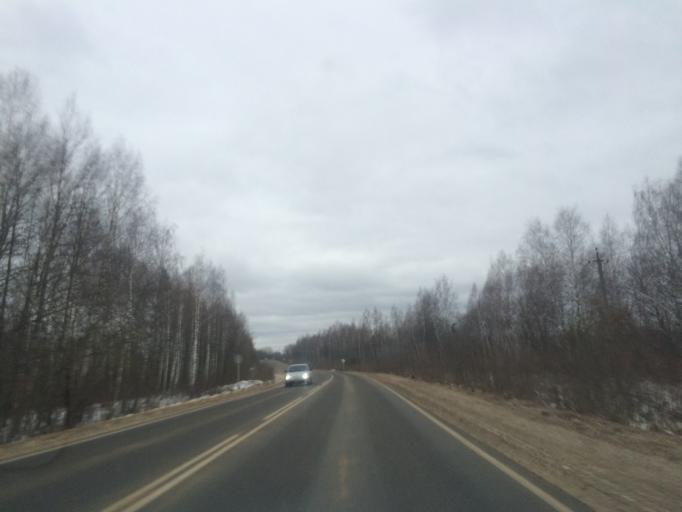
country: RU
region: Tula
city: Odoyev
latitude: 54.0016
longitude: 36.7621
